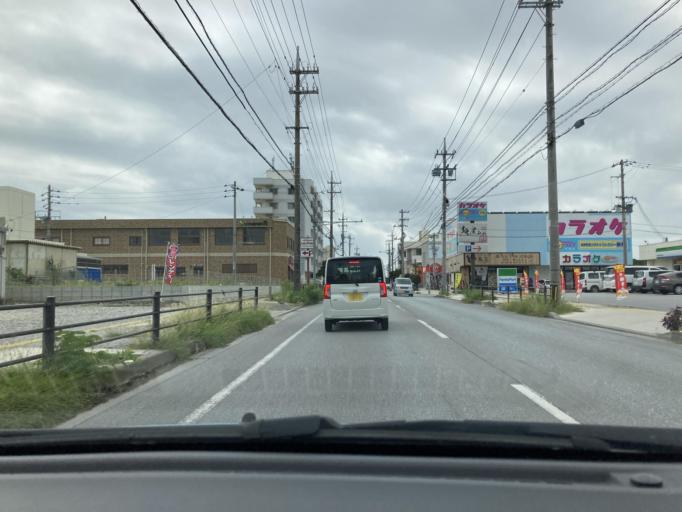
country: JP
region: Okinawa
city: Ginowan
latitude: 26.2449
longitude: 127.7689
